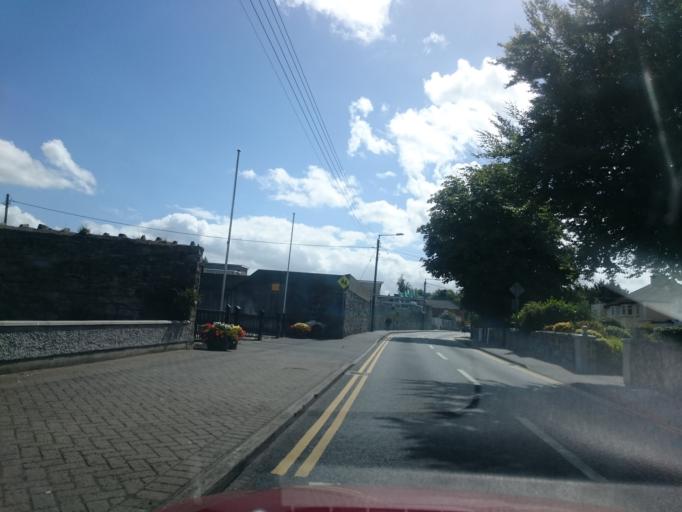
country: IE
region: Leinster
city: Clondalkin
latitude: 53.3188
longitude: -6.3948
